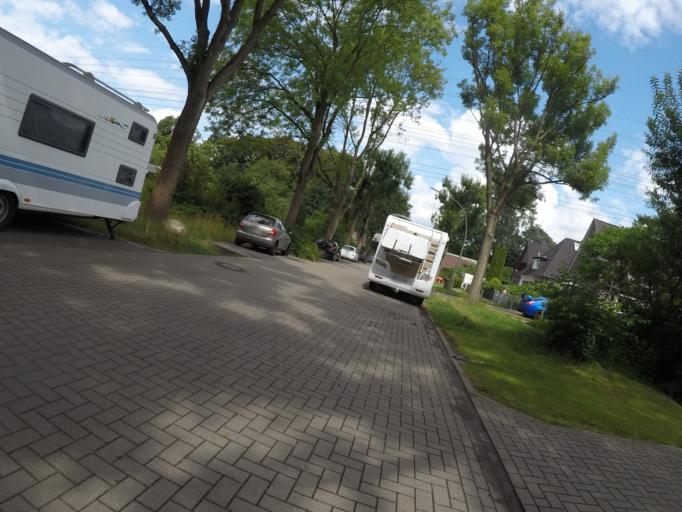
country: DE
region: Hamburg
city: Stellingen
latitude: 53.6062
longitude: 9.9390
